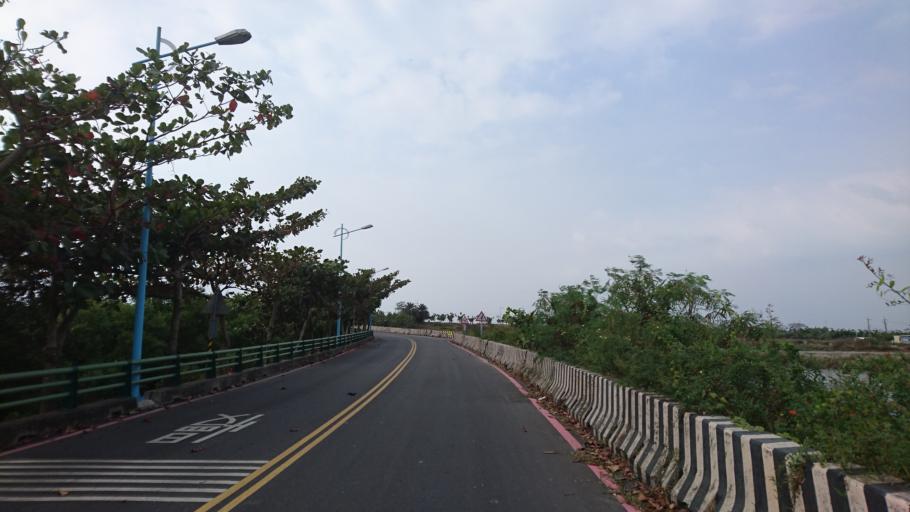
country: TW
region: Taiwan
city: Fengshan
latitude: 22.4327
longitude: 120.4910
